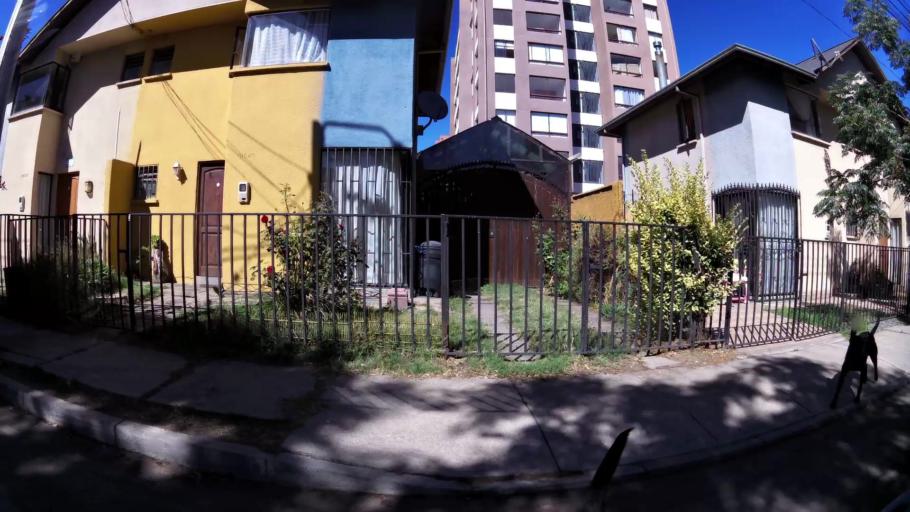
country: CL
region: O'Higgins
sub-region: Provincia de Cachapoal
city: Rancagua
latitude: -34.1740
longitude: -70.7015
